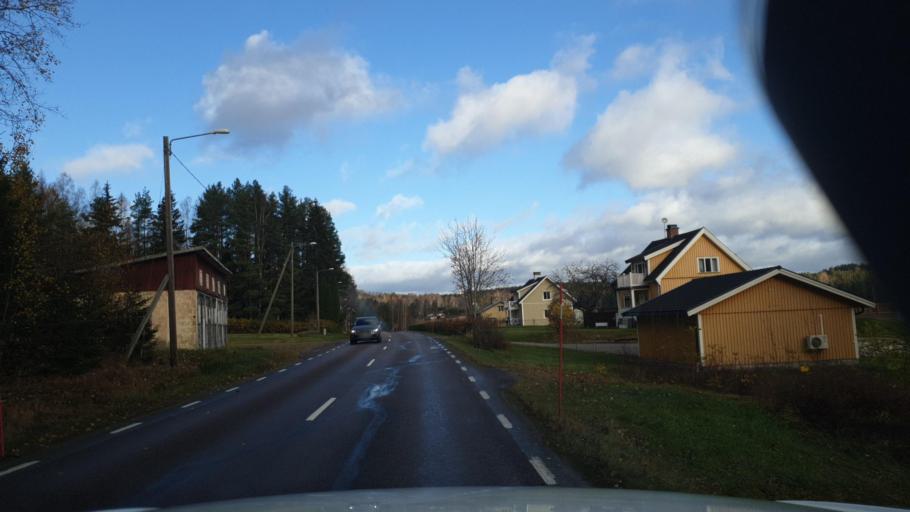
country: SE
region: Vaermland
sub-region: Grums Kommun
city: Slottsbron
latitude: 59.4504
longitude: 12.8831
